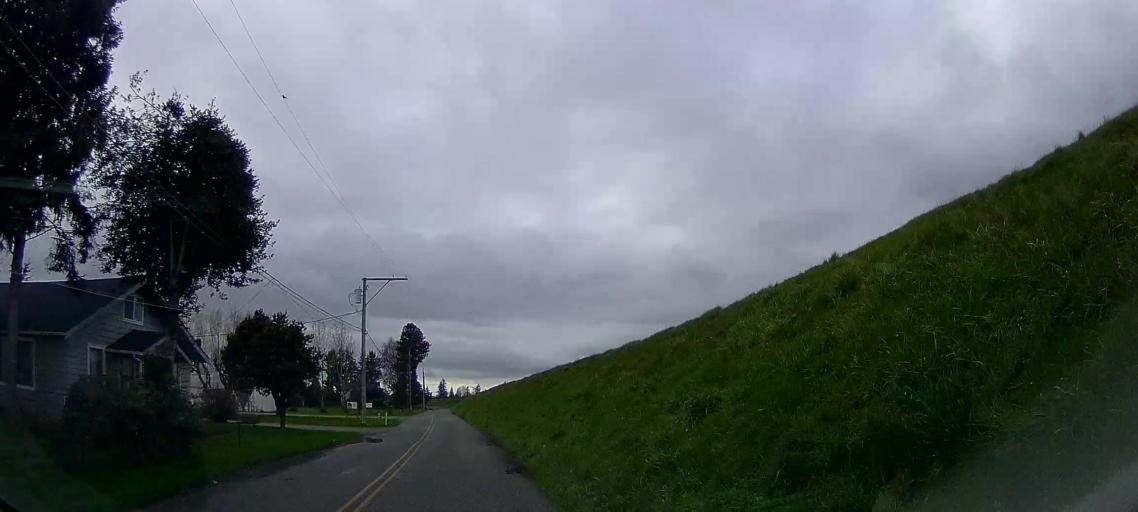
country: US
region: Washington
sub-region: Skagit County
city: Mount Vernon
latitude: 48.4464
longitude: -122.3626
